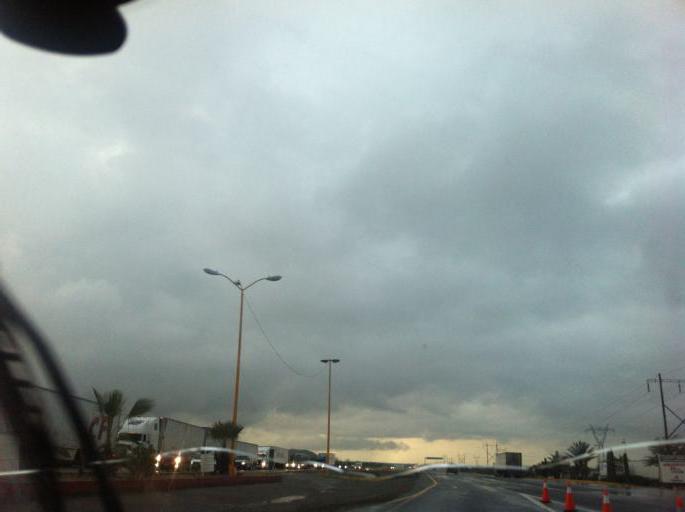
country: MX
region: Sonora
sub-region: Hermosillo
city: Estacion Zamora
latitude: 29.2210
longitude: -110.9302
